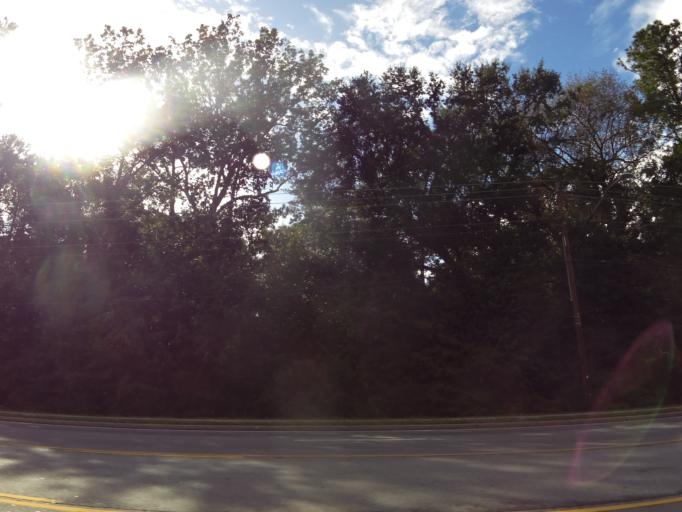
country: US
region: Georgia
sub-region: Liberty County
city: Hinesville
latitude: 31.8125
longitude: -81.6023
